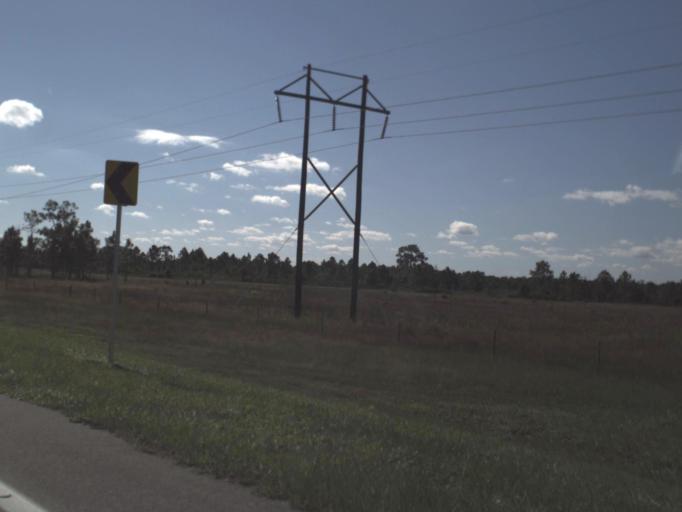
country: US
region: Florida
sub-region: Lee County
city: Lehigh Acres
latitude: 26.5363
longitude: -81.6315
